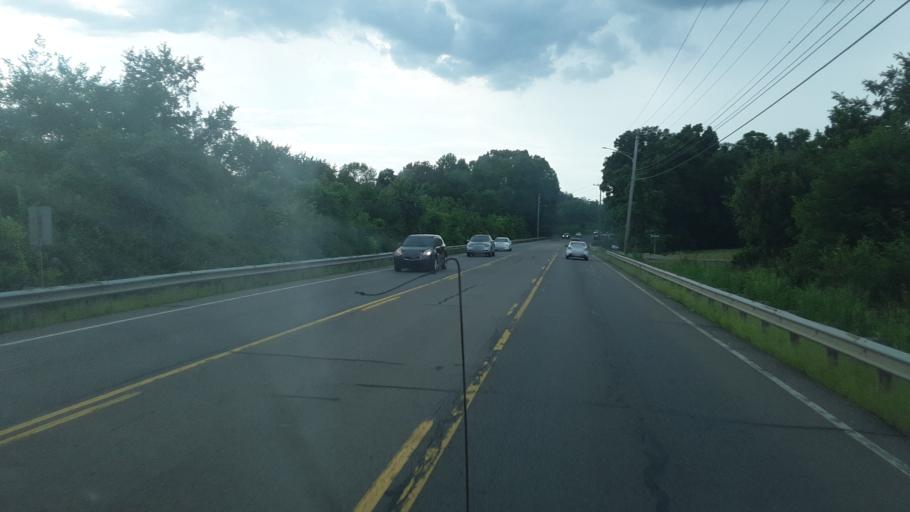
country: US
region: Tennessee
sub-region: Montgomery County
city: Clarksville
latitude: 36.5287
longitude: -87.2811
